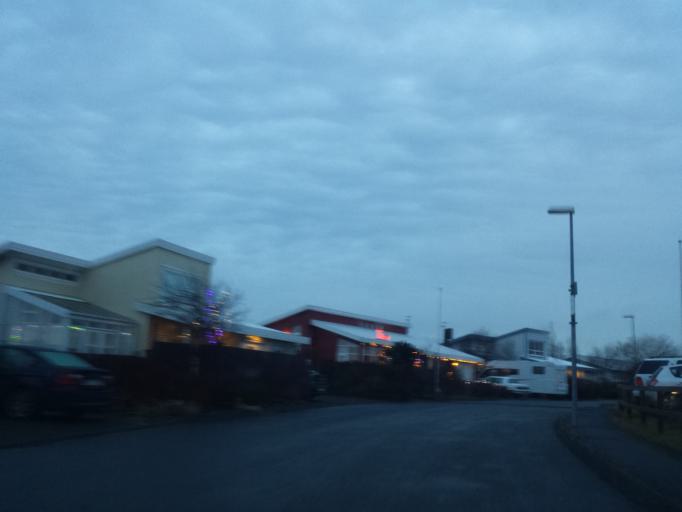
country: IS
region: Capital Region
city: Mosfellsbaer
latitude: 64.1367
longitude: -21.7760
